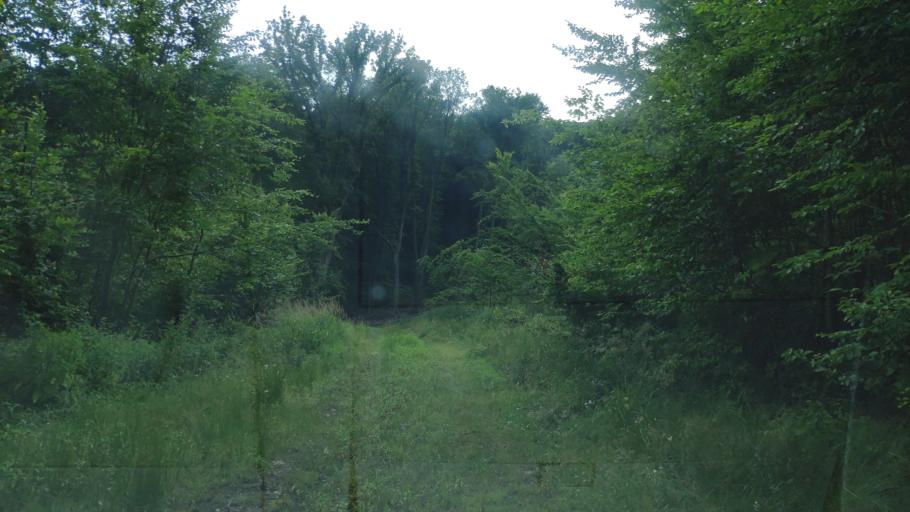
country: SK
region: Presovsky
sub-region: Okres Presov
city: Presov
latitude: 48.8744
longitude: 21.2199
